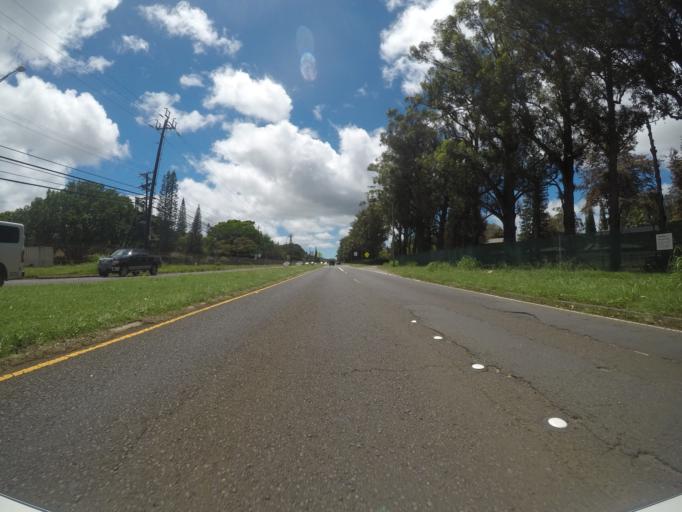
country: US
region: Hawaii
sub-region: Honolulu County
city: Schofield Barracks
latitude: 21.4901
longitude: -158.0443
